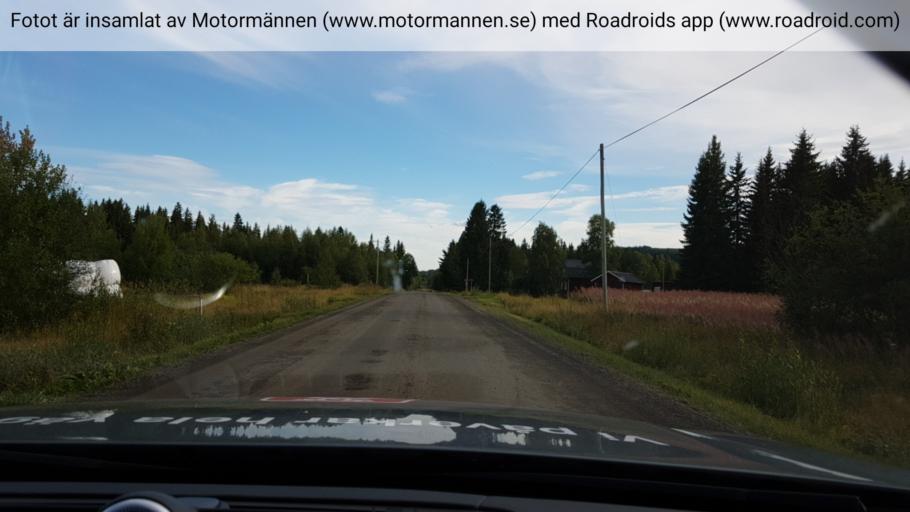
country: SE
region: Jaemtland
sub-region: Stroemsunds Kommun
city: Stroemsund
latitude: 64.0297
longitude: 15.8096
